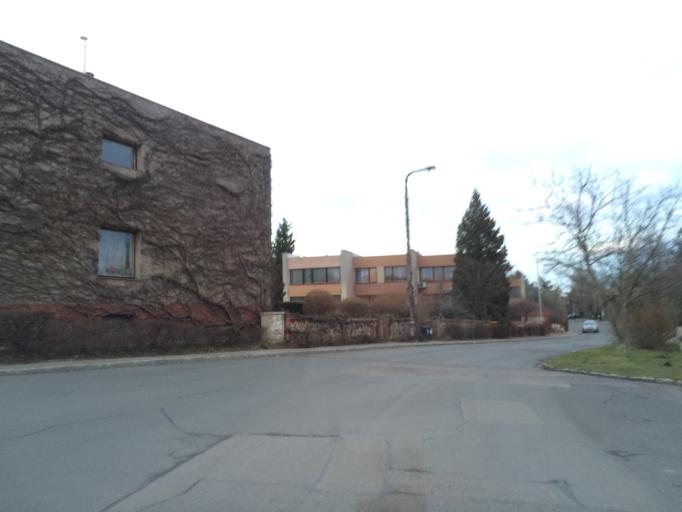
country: CZ
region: Praha
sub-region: Praha 1
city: Mala Strana
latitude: 50.1138
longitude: 14.3811
